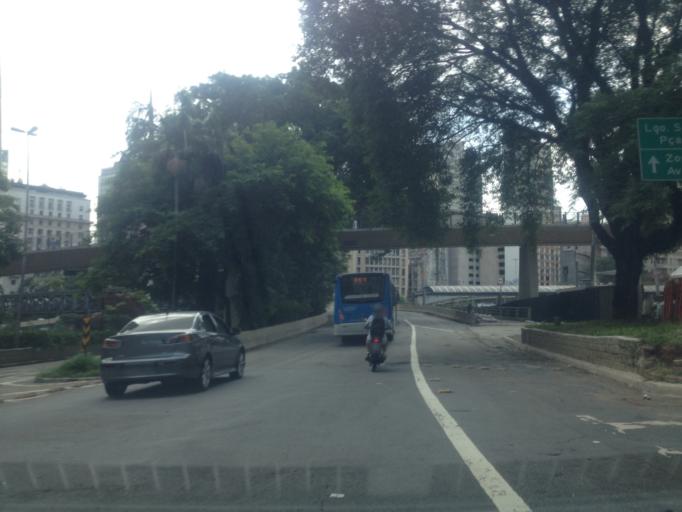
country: BR
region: Sao Paulo
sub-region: Sao Paulo
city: Sao Paulo
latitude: -23.5492
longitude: -46.6409
